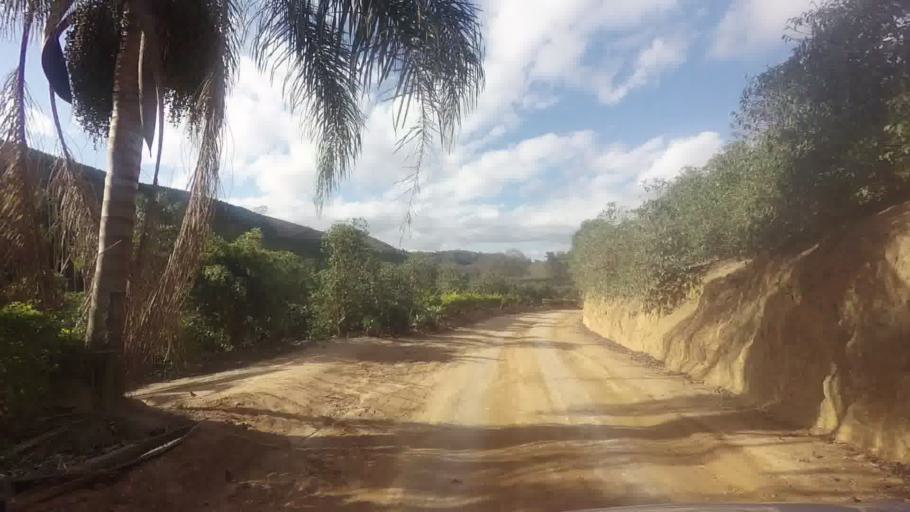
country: BR
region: Espirito Santo
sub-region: Sao Jose Do Calcado
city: Sao Jose do Calcado
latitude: -20.9814
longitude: -41.5140
